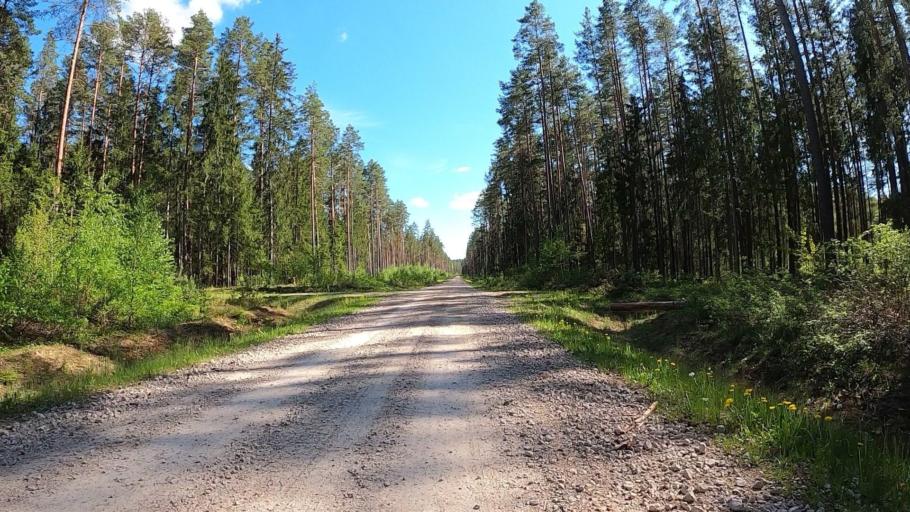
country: LV
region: Baldone
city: Baldone
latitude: 56.7809
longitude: 24.3741
